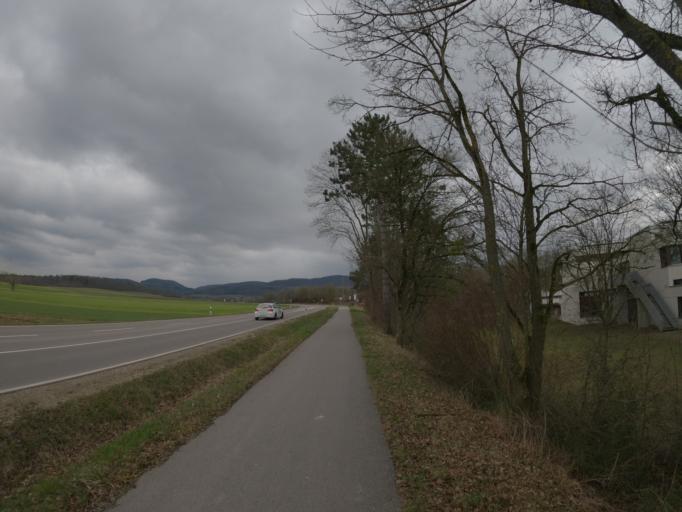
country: DE
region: Baden-Wuerttemberg
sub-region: Regierungsbezirk Stuttgart
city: Schlat
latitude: 48.6681
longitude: 9.6950
